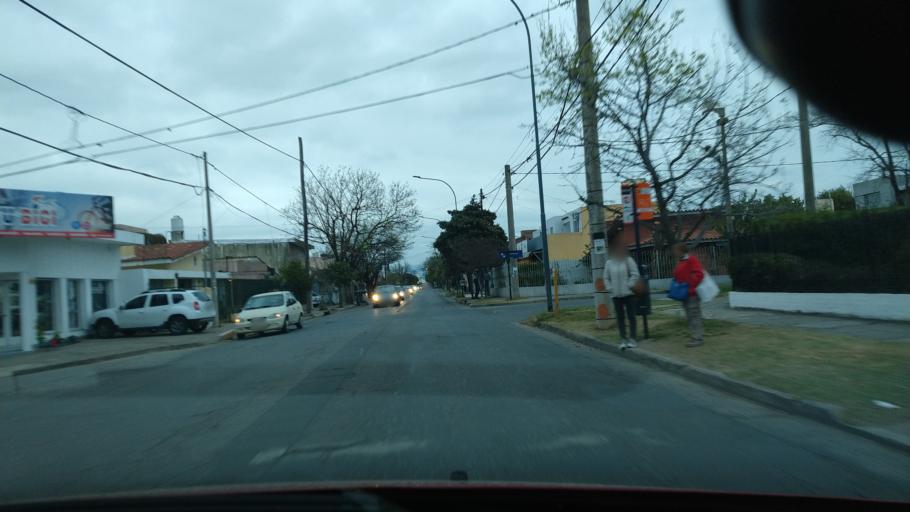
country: AR
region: Cordoba
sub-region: Departamento de Capital
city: Cordoba
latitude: -31.3598
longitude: -64.2348
